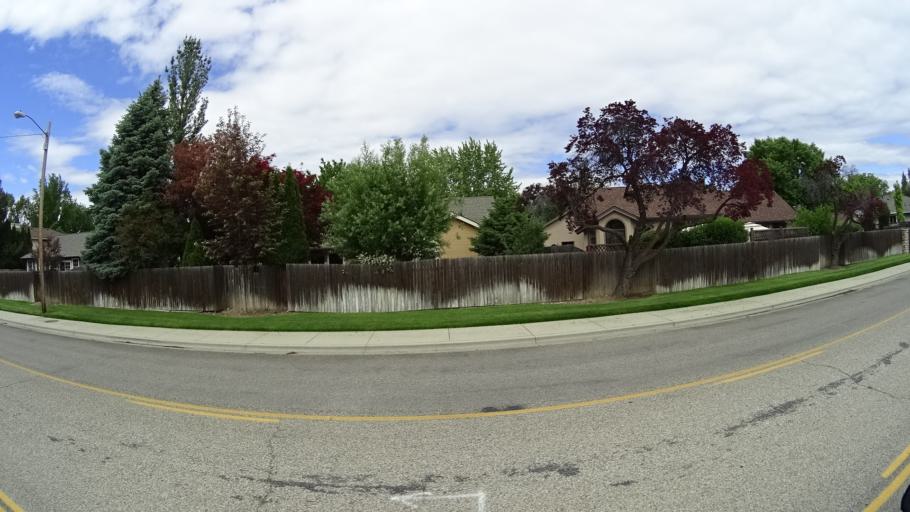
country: US
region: Idaho
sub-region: Ada County
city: Boise
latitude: 43.5707
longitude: -116.1734
